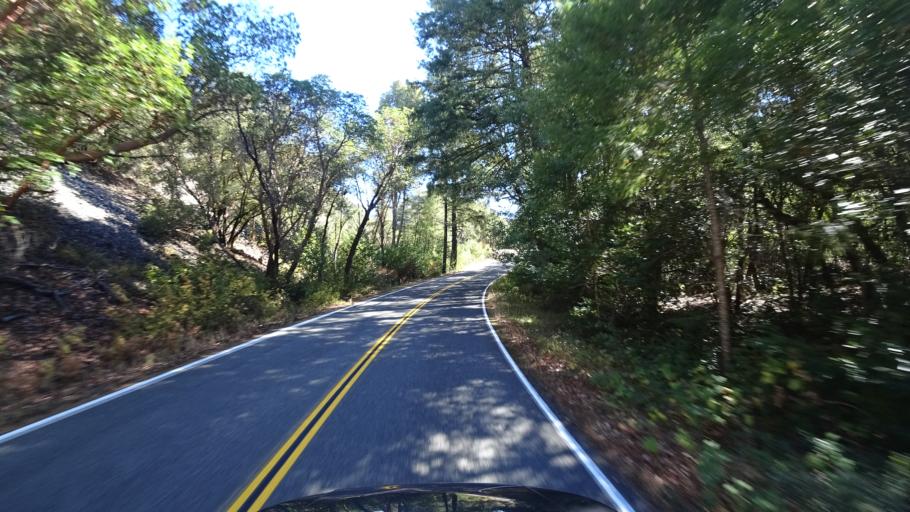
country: US
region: California
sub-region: Siskiyou County
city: Happy Camp
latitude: 41.3803
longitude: -123.4642
